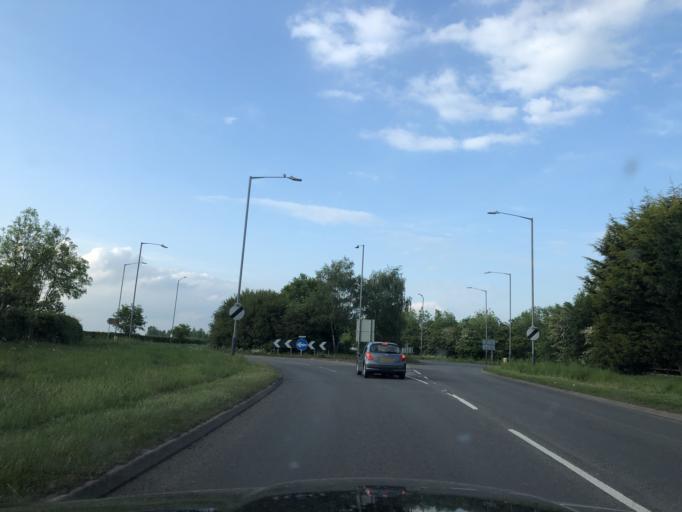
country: GB
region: England
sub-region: Warwickshire
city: Wellesbourne Mountford
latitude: 52.1990
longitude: -1.5992
